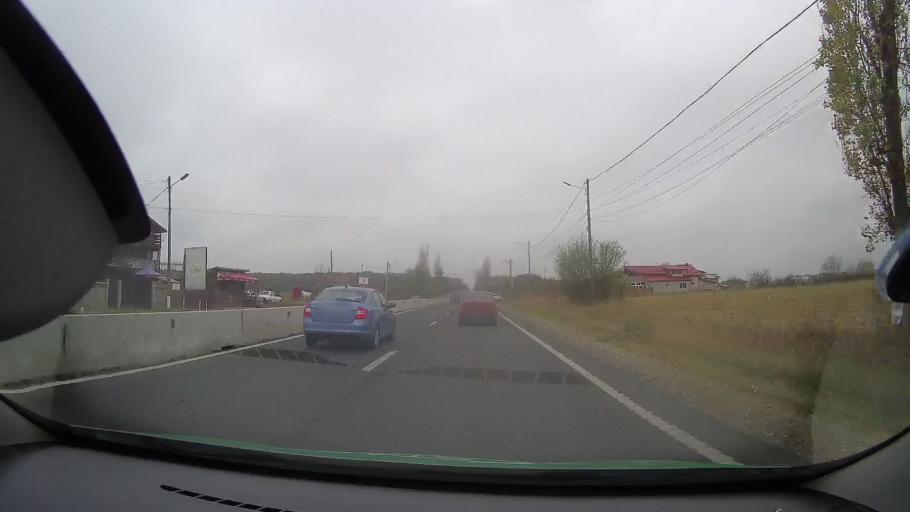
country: RO
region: Prahova
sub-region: Comuna Gorgota
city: Potigrafu
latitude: 44.7740
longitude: 26.1012
